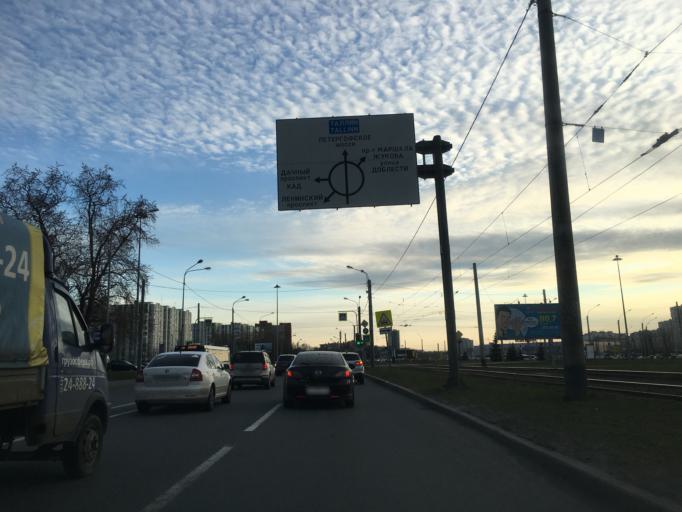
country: RU
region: St.-Petersburg
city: Dachnoye
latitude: 59.8528
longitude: 30.2393
